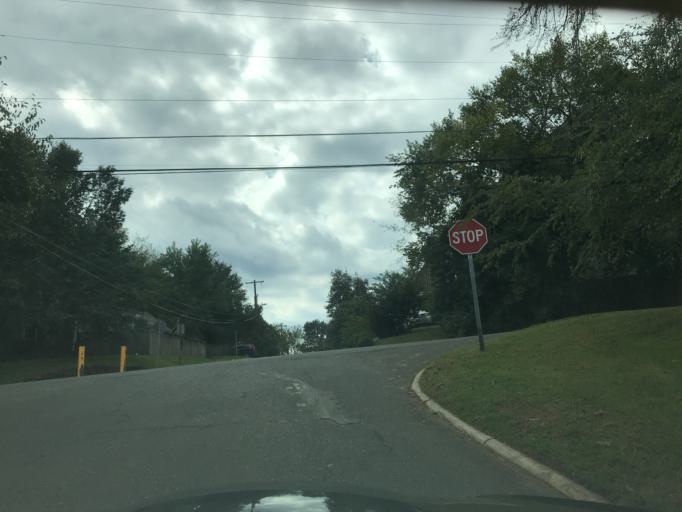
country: US
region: North Carolina
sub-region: Orange County
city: Chapel Hill
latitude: 35.9199
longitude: -79.0595
